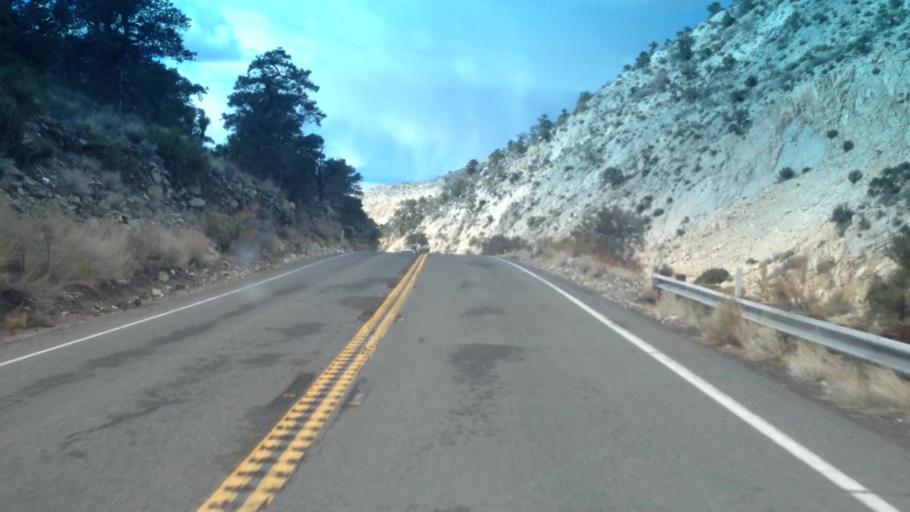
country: US
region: California
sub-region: San Bernardino County
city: Big Bear City
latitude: 34.3404
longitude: -116.8400
